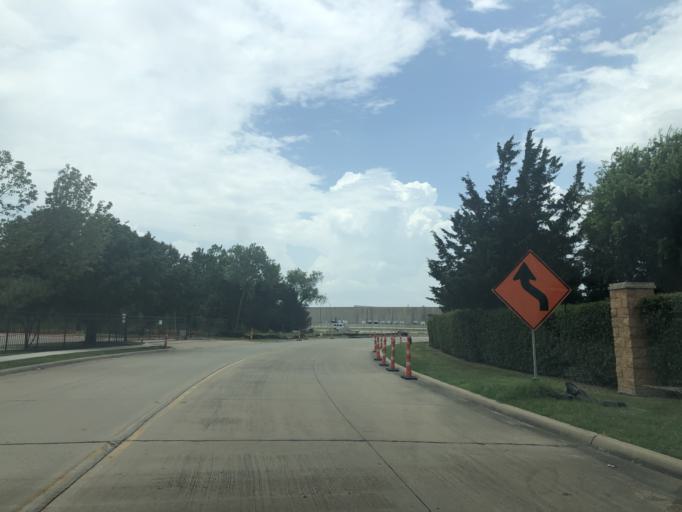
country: US
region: Texas
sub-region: Dallas County
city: Grand Prairie
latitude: 32.7340
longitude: -97.0179
